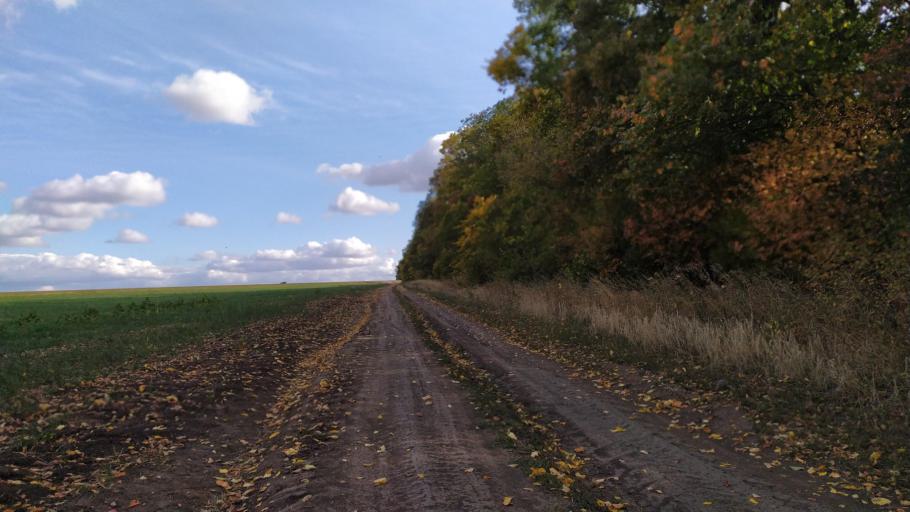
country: RU
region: Kursk
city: Kursk
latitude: 51.6190
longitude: 36.1628
